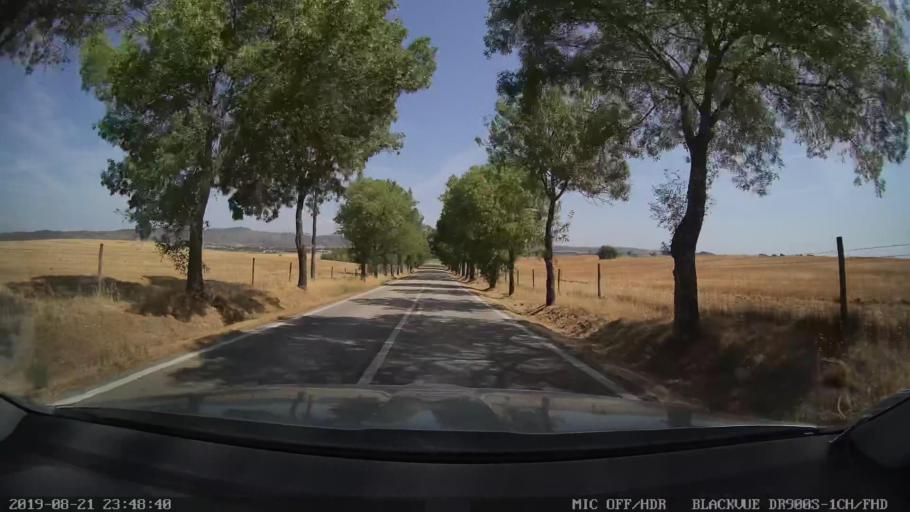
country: PT
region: Castelo Branco
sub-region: Idanha-A-Nova
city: Idanha-a-Nova
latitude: 39.8682
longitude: -7.2551
